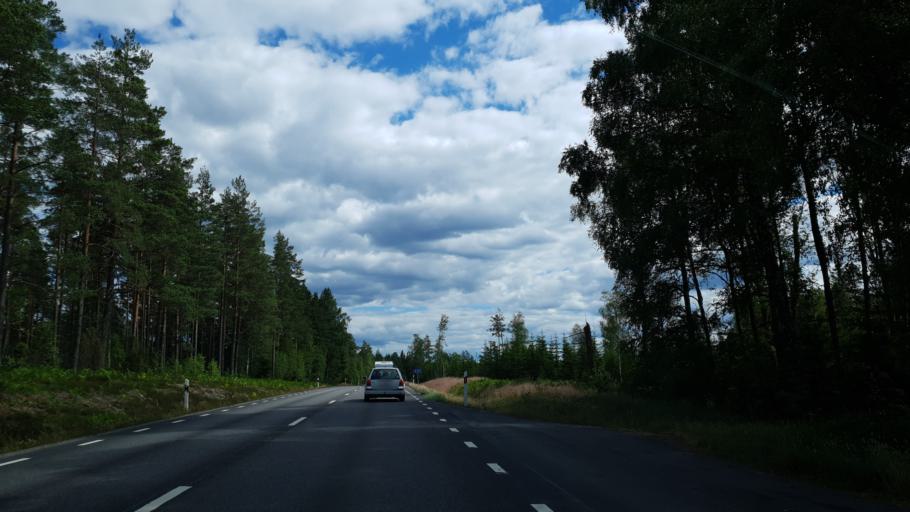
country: SE
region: Kronoberg
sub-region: Lessebo Kommun
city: Lessebo
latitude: 56.8285
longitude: 15.4000
